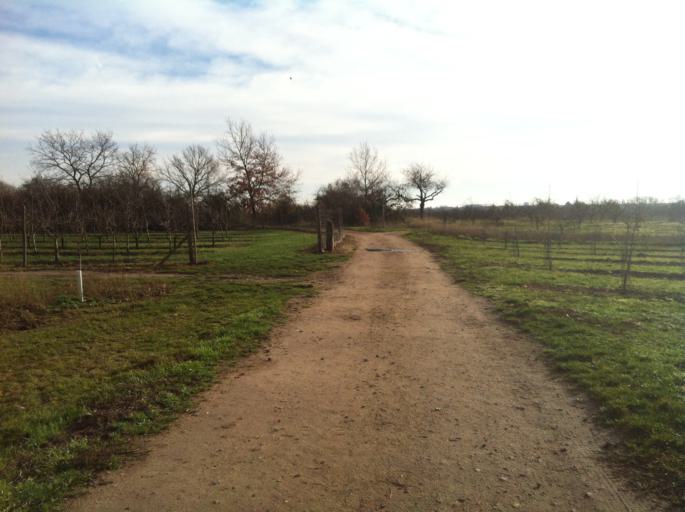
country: DE
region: Rheinland-Pfalz
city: Budenheim
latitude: 49.9969
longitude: 8.1656
